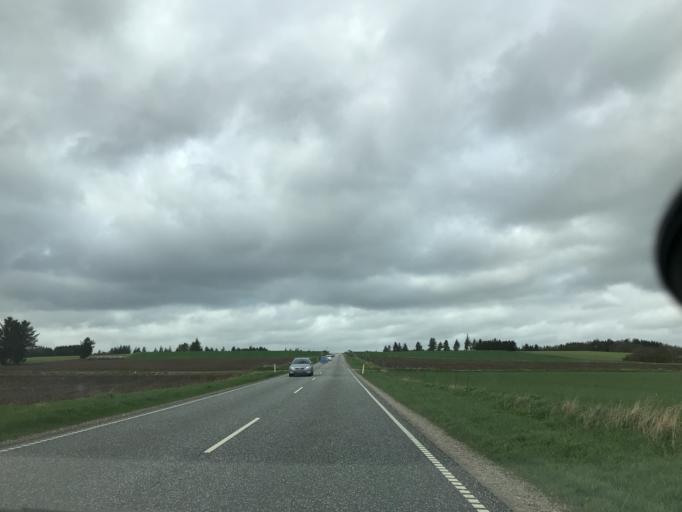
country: DK
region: Central Jutland
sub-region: Skive Kommune
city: Skive
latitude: 56.5023
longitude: 8.9553
